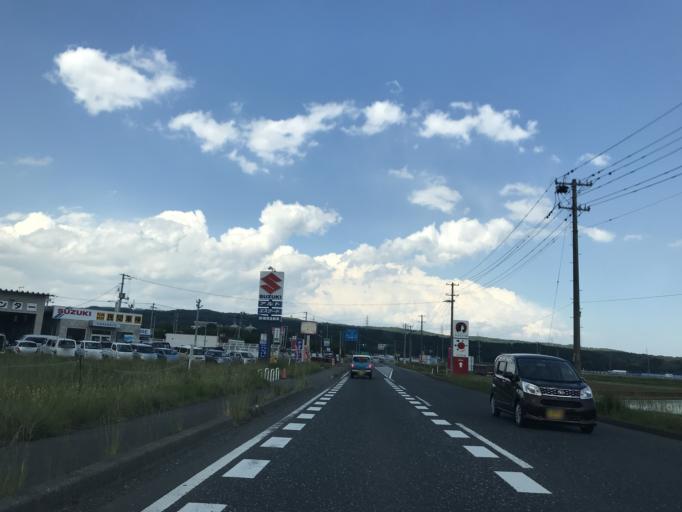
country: JP
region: Miyagi
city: Wakuya
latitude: 38.5344
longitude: 141.1458
